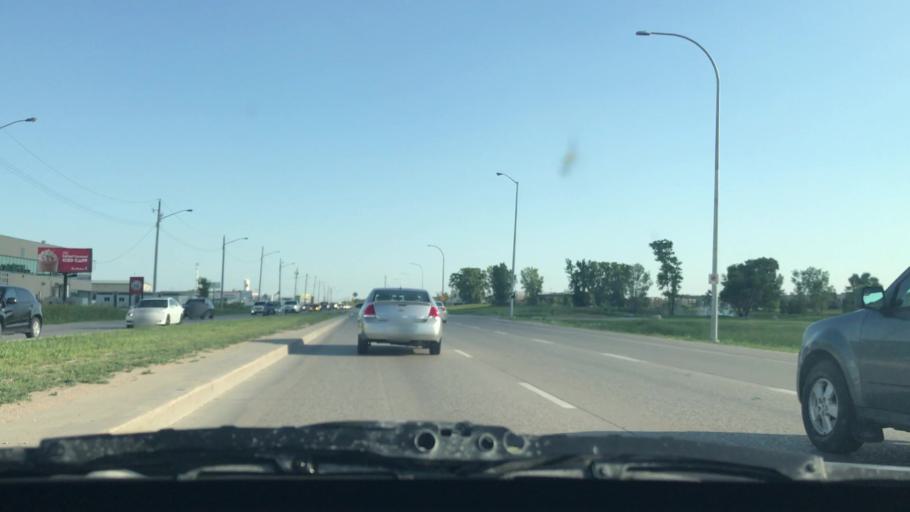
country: CA
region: Manitoba
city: Winnipeg
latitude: 49.8373
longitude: -97.2093
